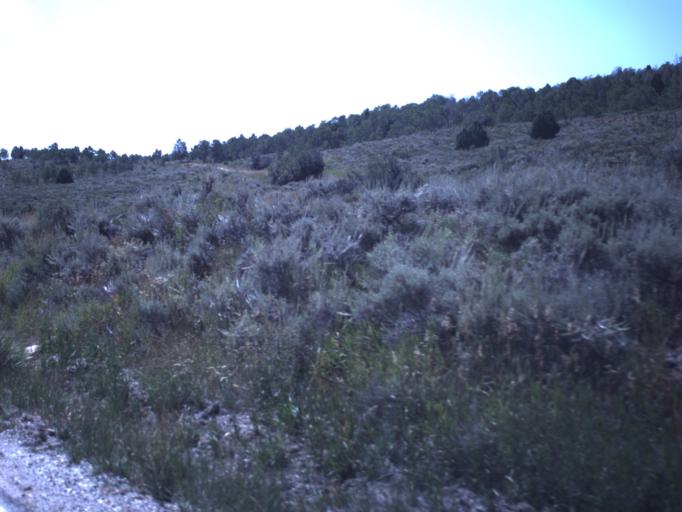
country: US
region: Utah
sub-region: Cache County
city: Richmond
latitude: 41.8669
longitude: -111.5699
